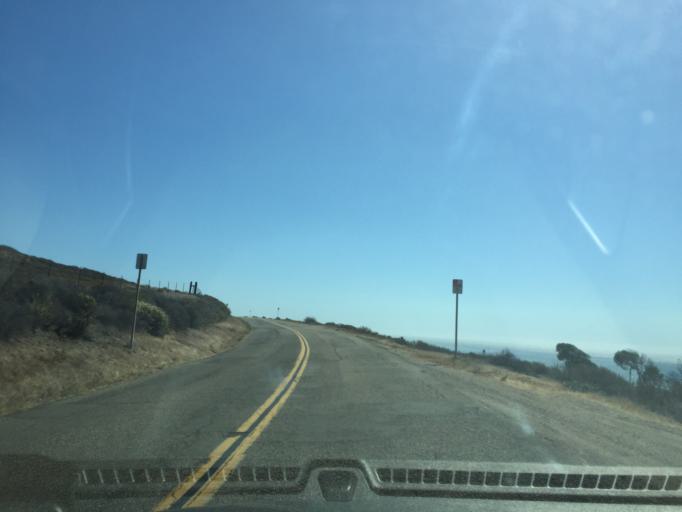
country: US
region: California
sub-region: Santa Barbara County
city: Lompoc
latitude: 34.5068
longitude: -120.4991
